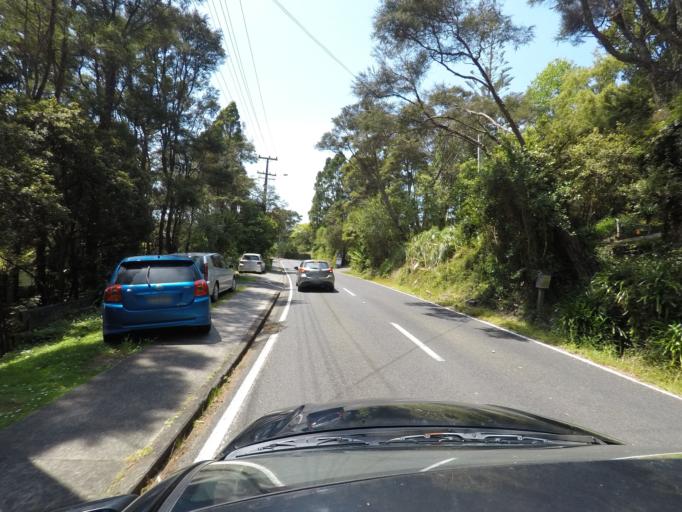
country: NZ
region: Auckland
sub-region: Auckland
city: Titirangi
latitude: -36.9584
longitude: 174.6393
